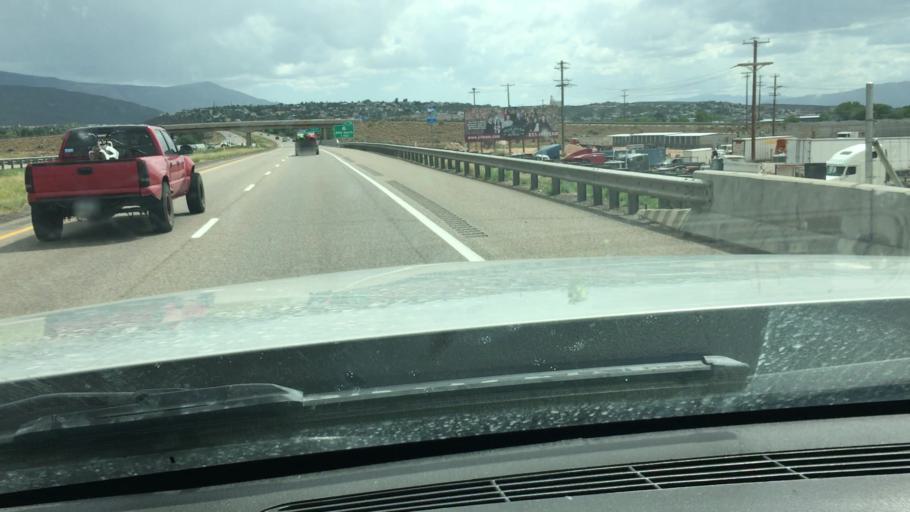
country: US
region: Utah
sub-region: Iron County
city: Cedar City
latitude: 37.6974
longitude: -113.0766
